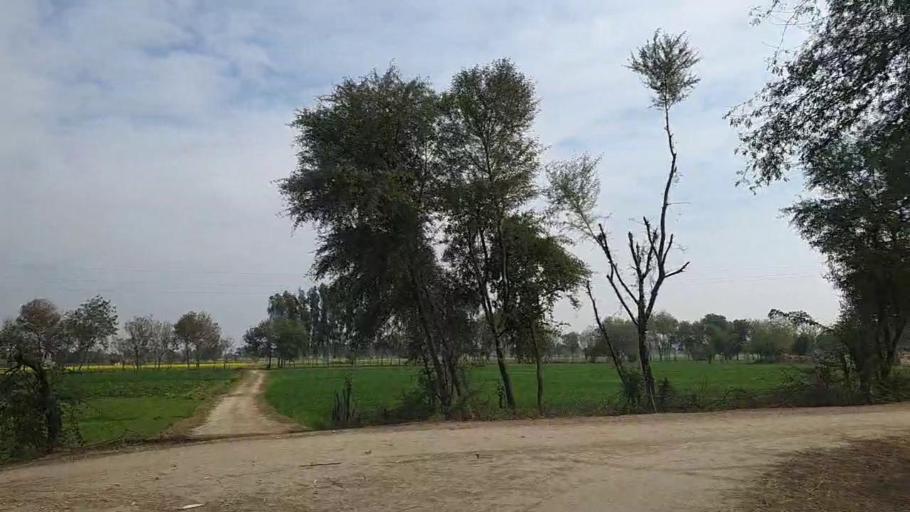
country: PK
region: Sindh
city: Nawabshah
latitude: 26.3760
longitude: 68.4450
